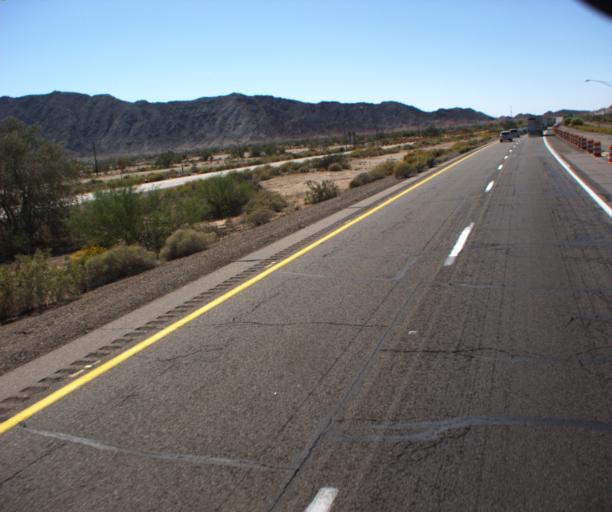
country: US
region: Arizona
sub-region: Yuma County
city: Wellton
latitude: 32.7308
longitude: -113.7177
